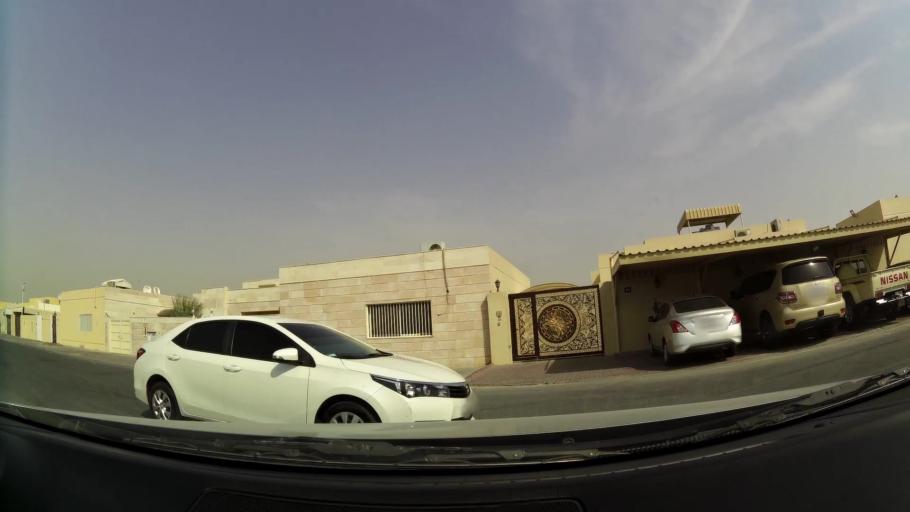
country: AE
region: Ash Shariqah
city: Sharjah
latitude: 25.2576
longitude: 55.4371
